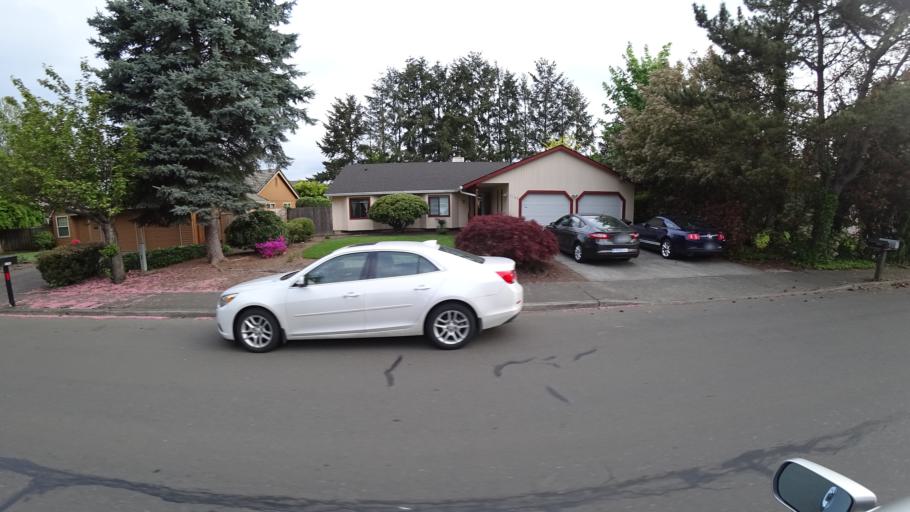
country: US
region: Oregon
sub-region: Washington County
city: Aloha
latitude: 45.5028
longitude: -122.9294
